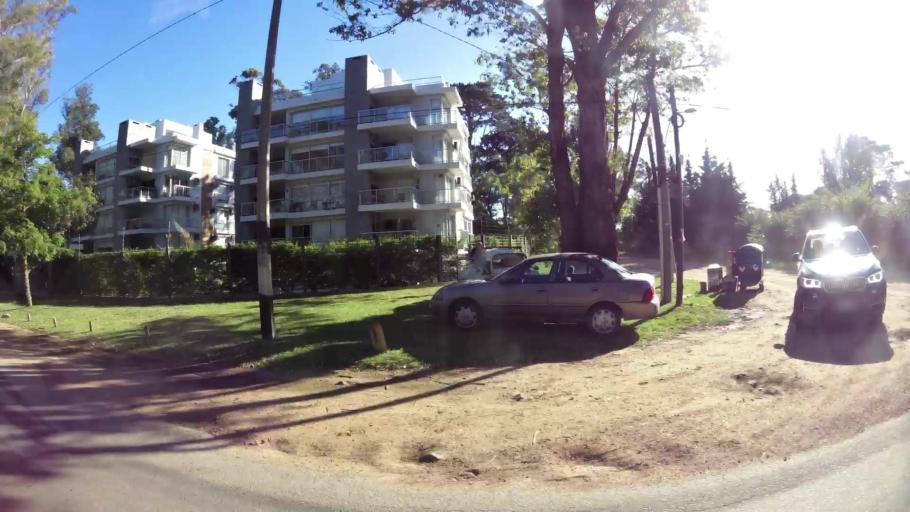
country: UY
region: Canelones
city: Paso de Carrasco
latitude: -34.8555
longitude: -56.0353
